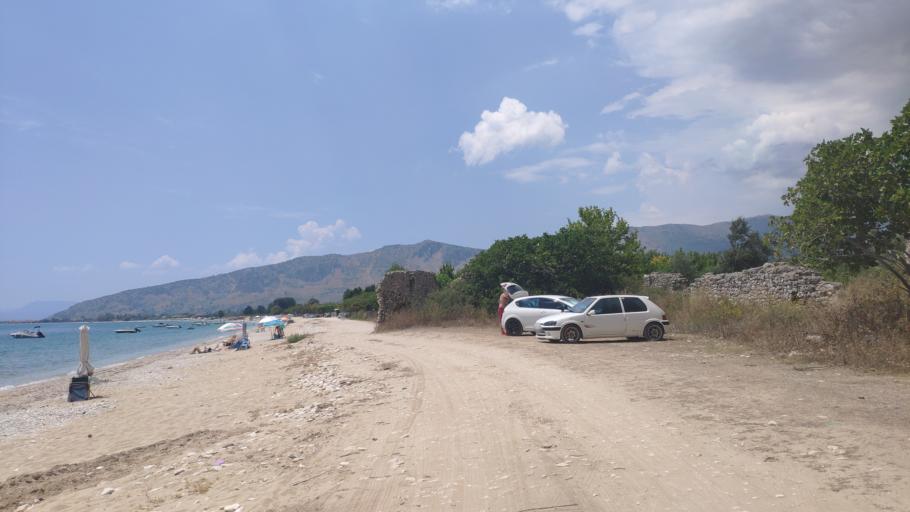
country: GR
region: West Greece
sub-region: Nomos Aitolias kai Akarnanias
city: Kandila
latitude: 38.6722
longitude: 20.9821
